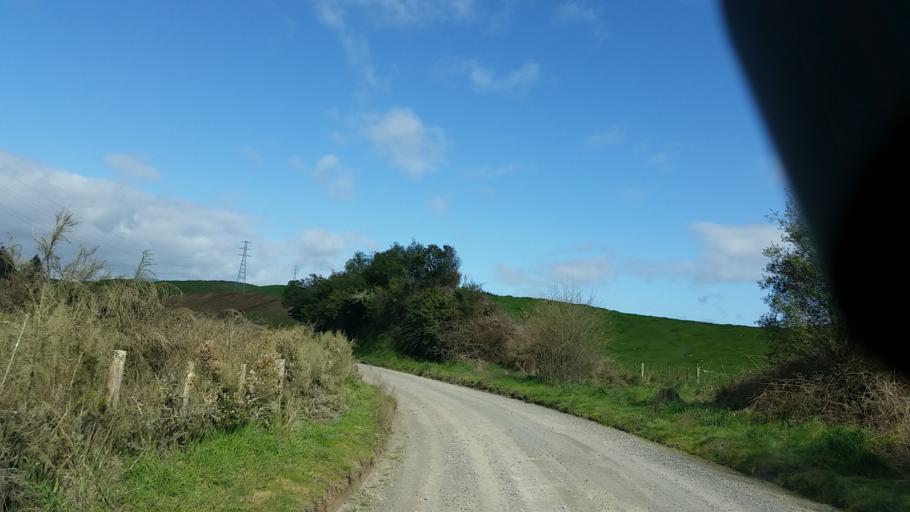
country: NZ
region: Waikato
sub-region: South Waikato District
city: Tokoroa
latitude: -38.3630
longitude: 176.0908
